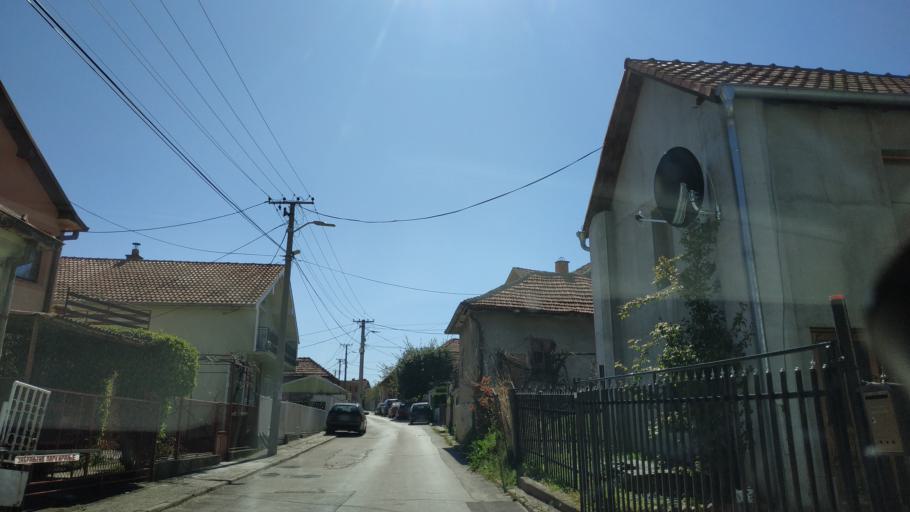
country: RS
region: Central Serbia
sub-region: Nisavski Okrug
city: Aleksinac
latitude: 43.5408
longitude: 21.7043
